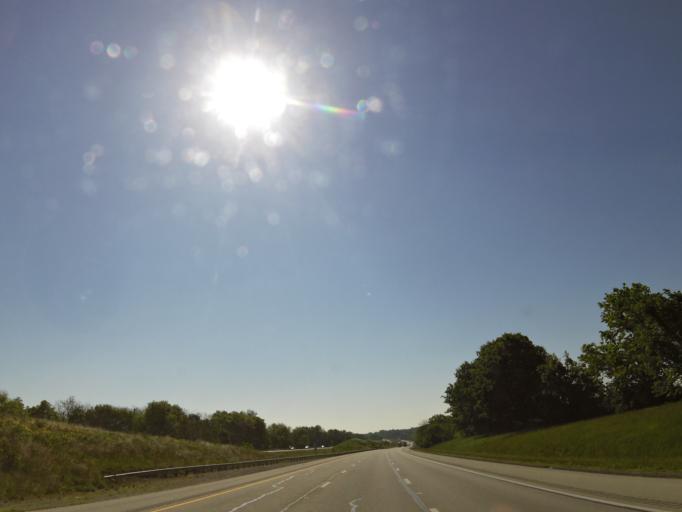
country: US
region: Kentucky
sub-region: Shelby County
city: Shelbyville
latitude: 38.1628
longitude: -85.1045
